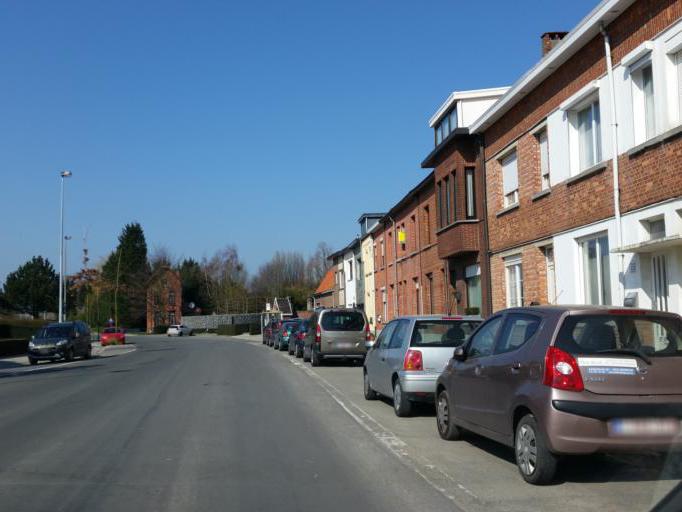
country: BE
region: Flanders
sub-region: Provincie Oost-Vlaanderen
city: Kruibeke
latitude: 51.1294
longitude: 4.2863
